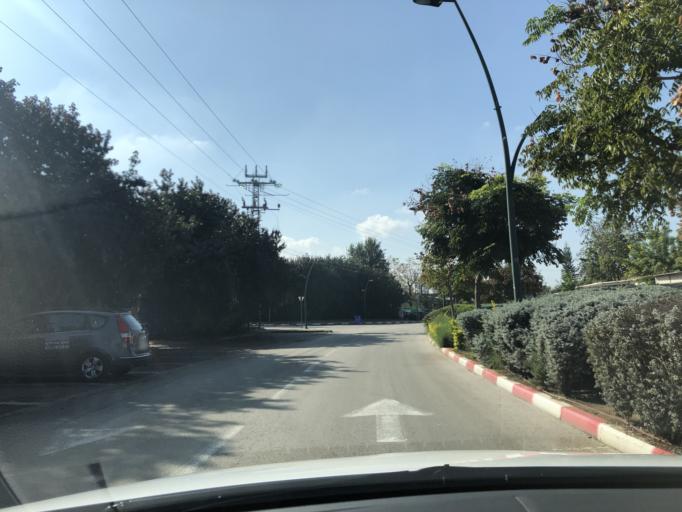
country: IL
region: Tel Aviv
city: Ramat HaSharon
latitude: 32.1267
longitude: 34.8555
